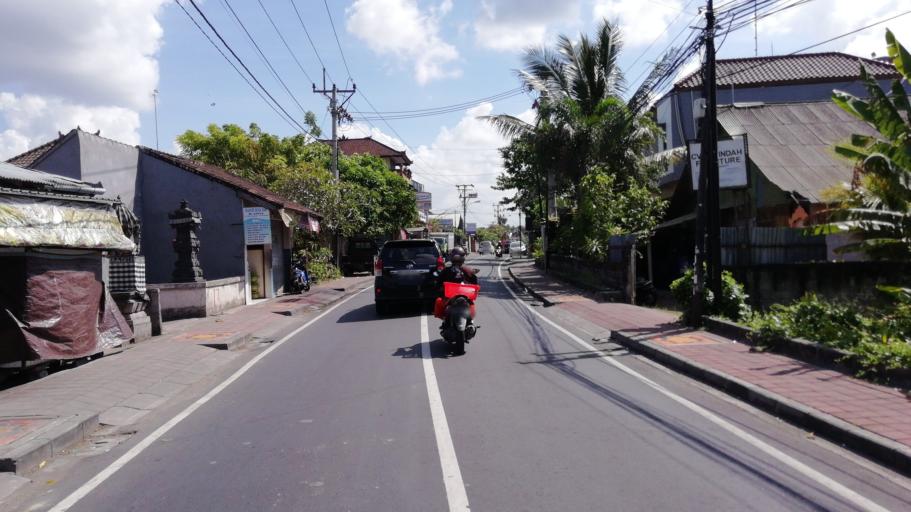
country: ID
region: Bali
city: Denpasar
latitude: -8.6545
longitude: 115.1724
